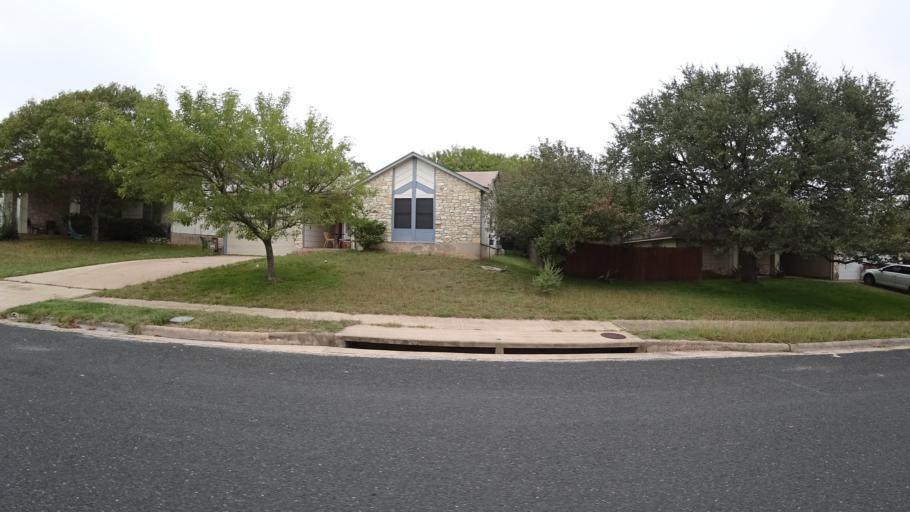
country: US
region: Texas
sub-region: Travis County
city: Barton Creek
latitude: 30.2397
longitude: -97.8951
